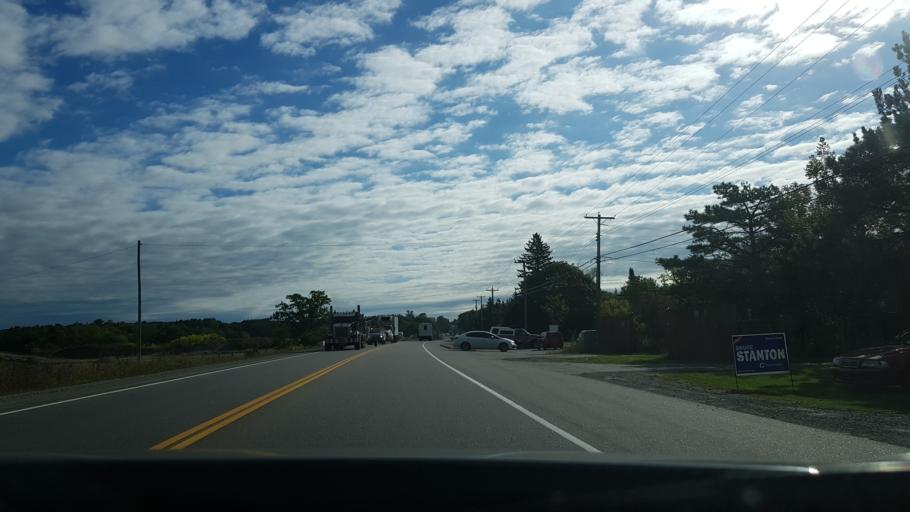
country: CA
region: Ontario
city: Orillia
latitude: 44.6150
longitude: -79.4943
